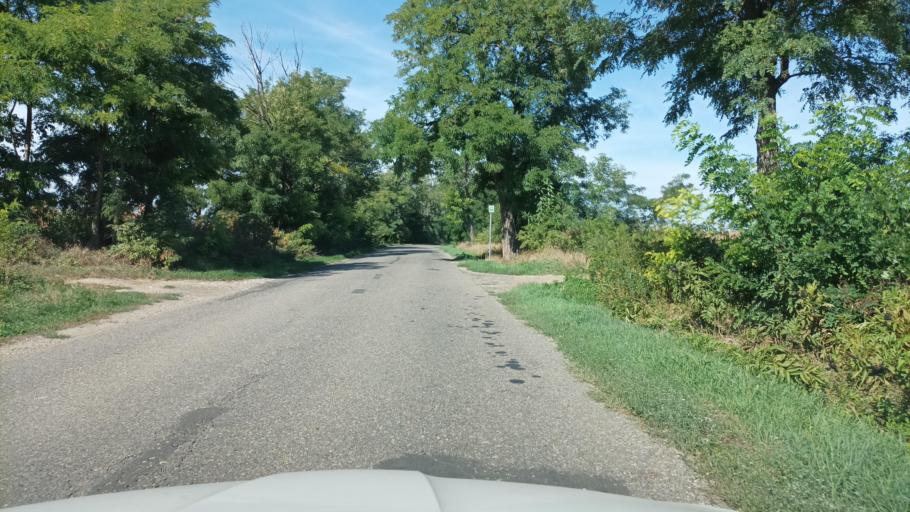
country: HU
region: Pest
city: Vacszentlaszlo
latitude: 47.5577
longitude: 19.5670
